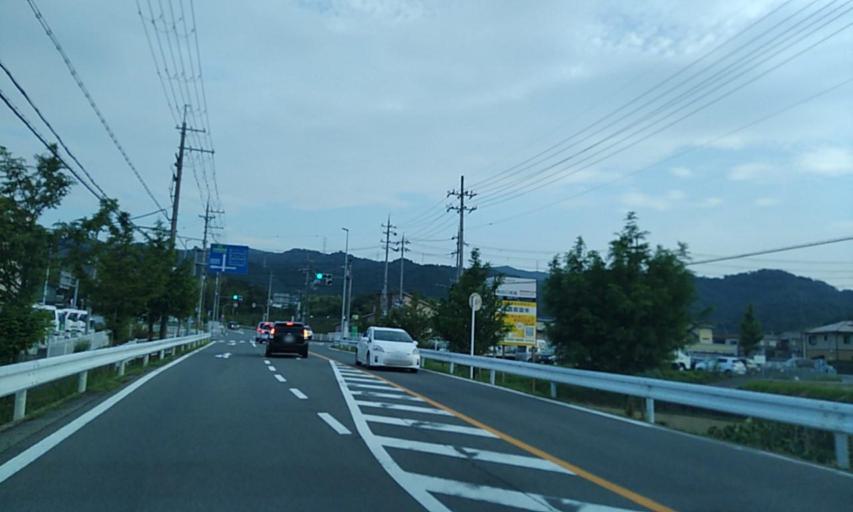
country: JP
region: Kyoto
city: Kameoka
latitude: 34.9971
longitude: 135.6048
